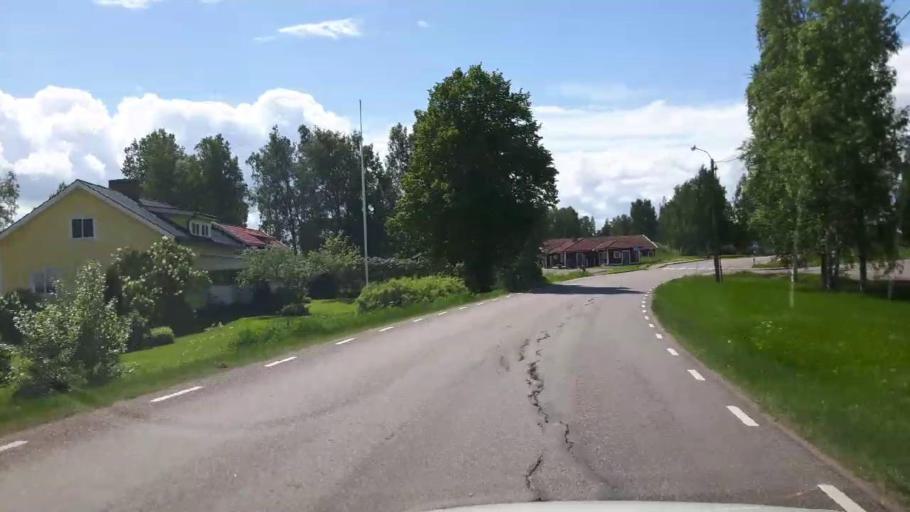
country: SE
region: Dalarna
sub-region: Faluns Kommun
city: Falun
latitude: 60.5958
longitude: 15.7640
